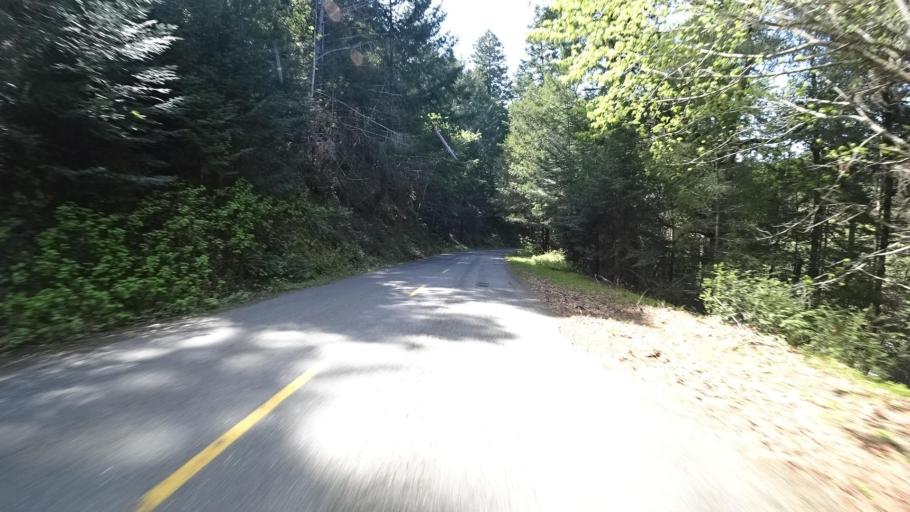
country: US
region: California
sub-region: Humboldt County
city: Redway
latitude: 40.3326
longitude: -123.6768
